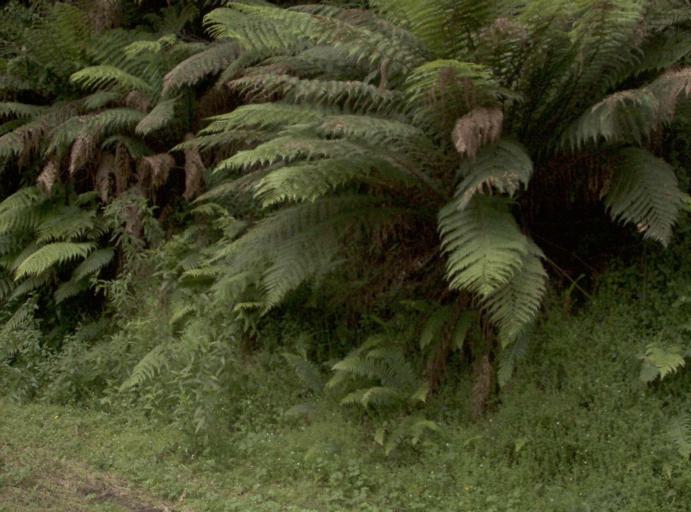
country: AU
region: Victoria
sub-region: Latrobe
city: Traralgon
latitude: -38.4586
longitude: 146.5465
